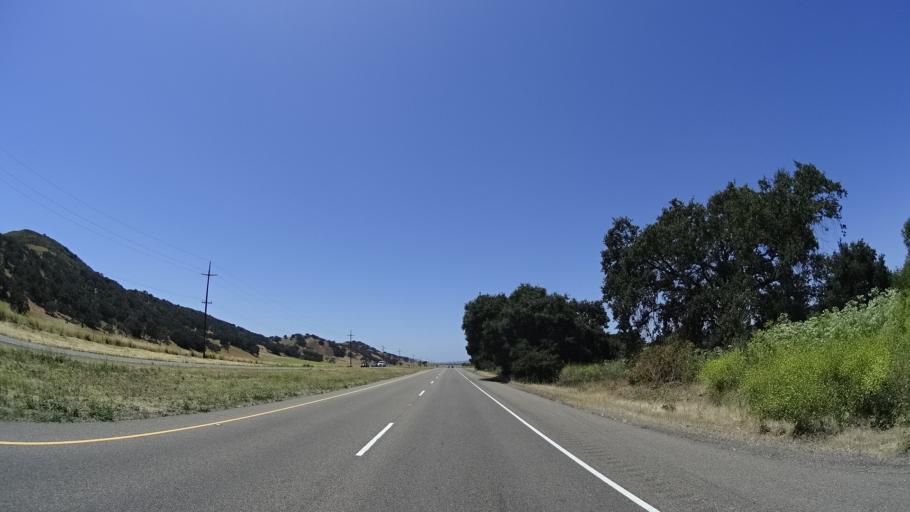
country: US
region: California
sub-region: Santa Barbara County
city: Los Alamos
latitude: 34.7247
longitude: -120.2168
